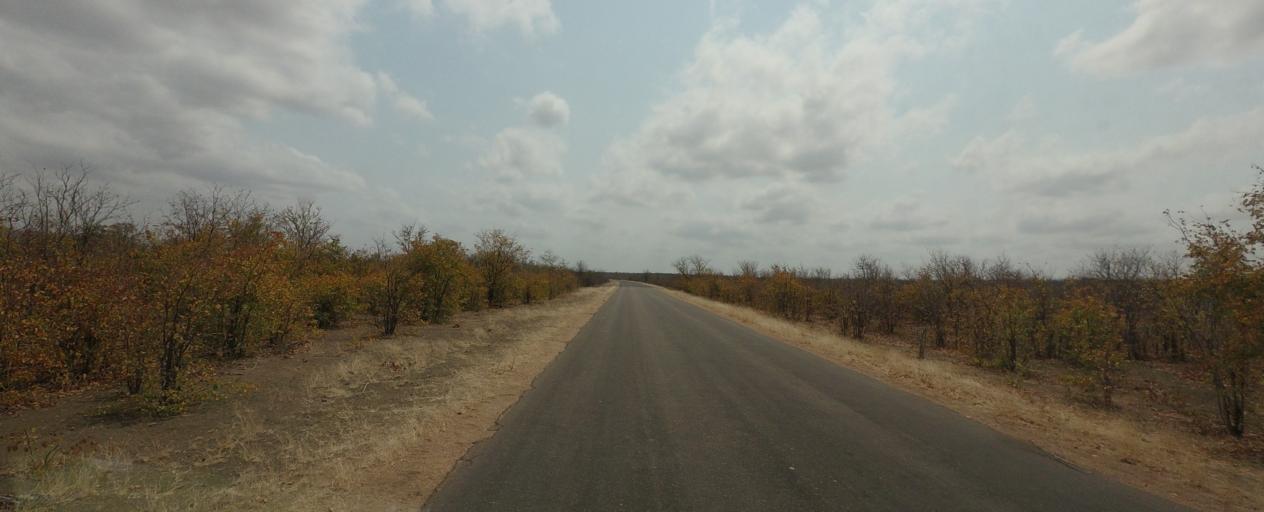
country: ZA
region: Limpopo
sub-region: Mopani District Municipality
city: Phalaborwa
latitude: -23.6023
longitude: 31.4548
